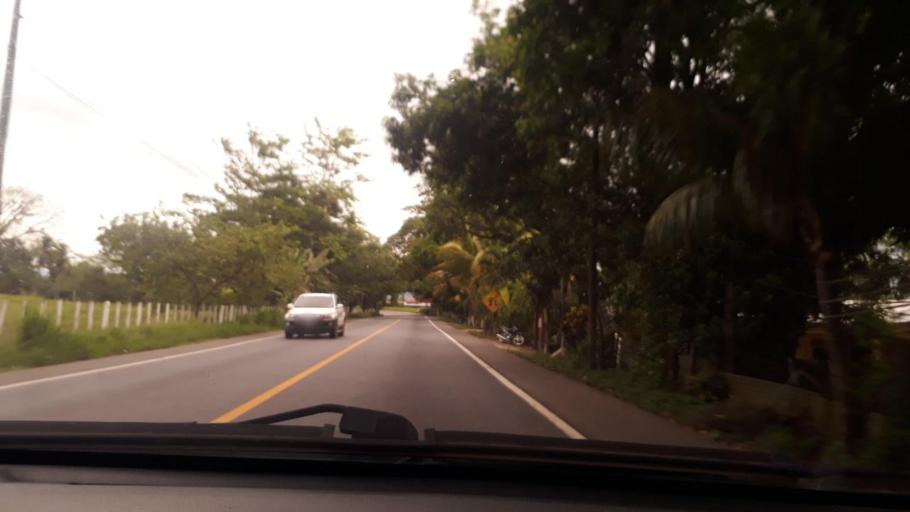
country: GT
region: Izabal
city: Morales
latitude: 15.4818
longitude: -88.8741
